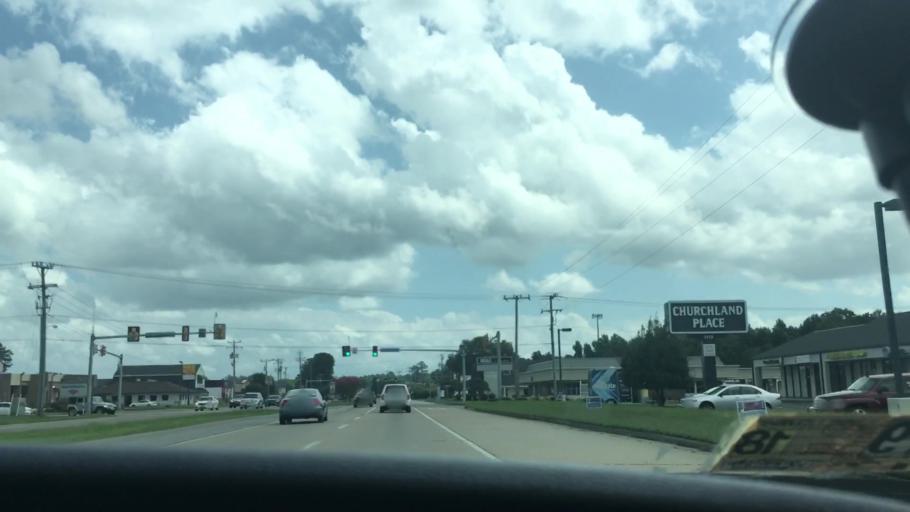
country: US
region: Virginia
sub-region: City of Portsmouth
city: Portsmouth Heights
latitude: 36.8625
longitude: -76.4022
